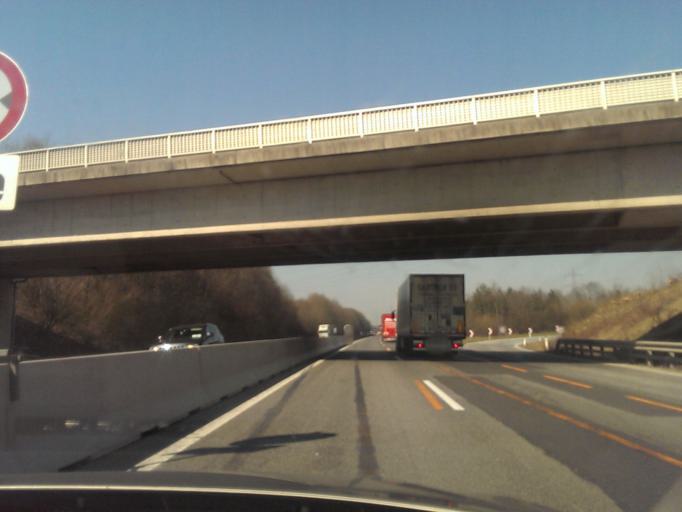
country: AT
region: Upper Austria
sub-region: Politischer Bezirk Vocklabruck
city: Wolfsegg am Hausruck
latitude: 48.1990
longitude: 13.6415
